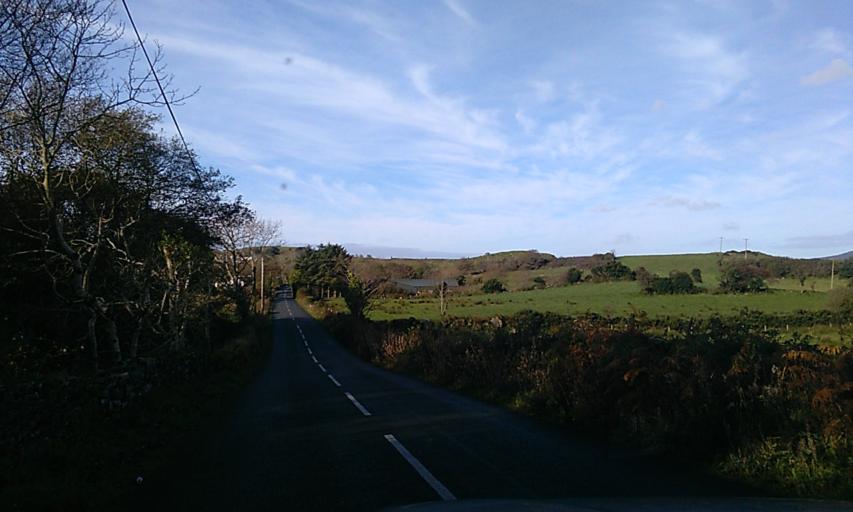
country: IE
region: Ulster
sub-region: County Donegal
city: Moville
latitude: 55.2794
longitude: -7.1192
